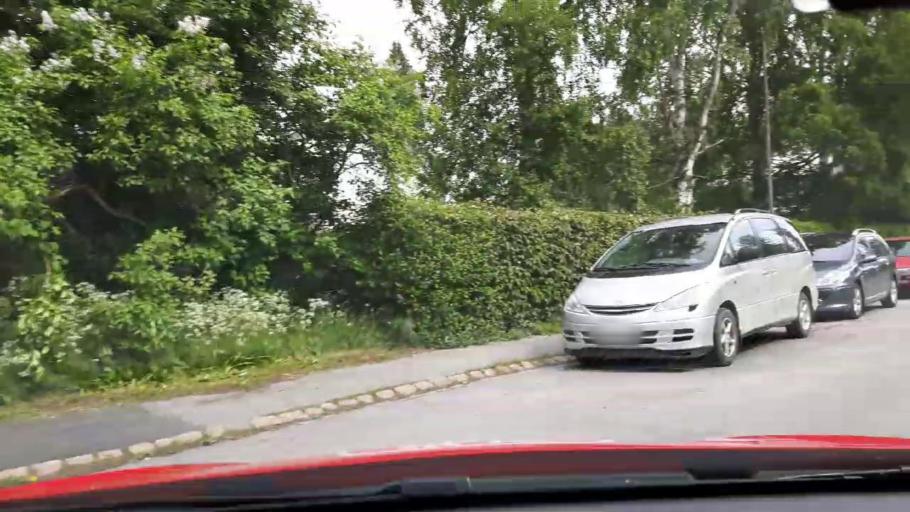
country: SE
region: Jaemtland
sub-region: OEstersunds Kommun
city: Ostersund
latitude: 63.1477
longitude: 14.4811
